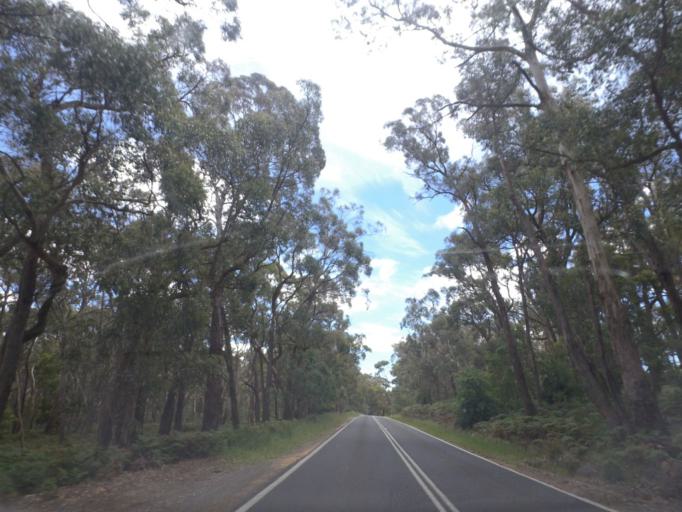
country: AU
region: Victoria
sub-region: Mount Alexander
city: Castlemaine
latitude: -37.3261
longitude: 144.1640
